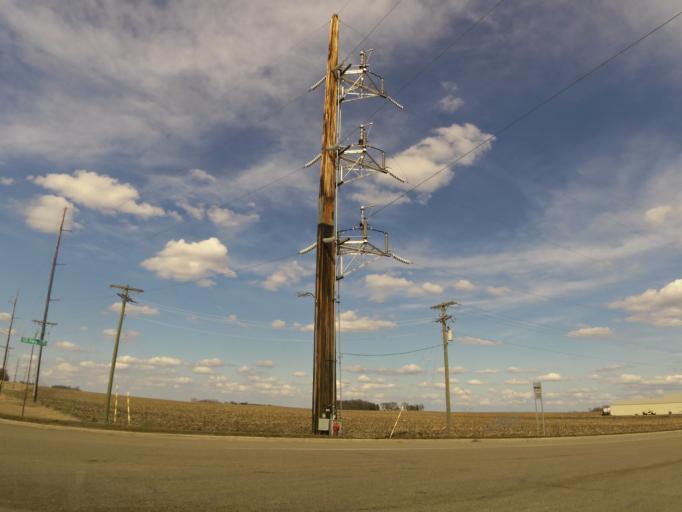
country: US
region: Minnesota
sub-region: Lac qui Parle County
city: Dawson
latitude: 44.9357
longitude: -96.0630
